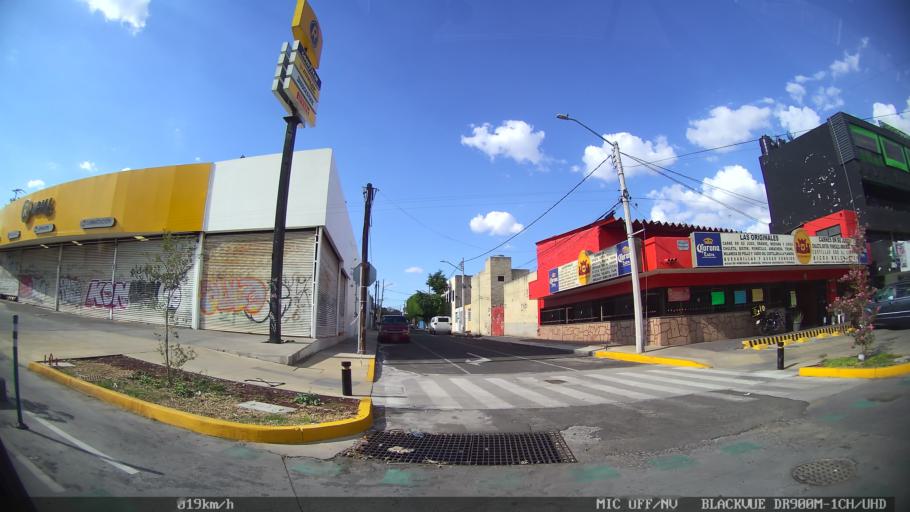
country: MX
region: Jalisco
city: Tlaquepaque
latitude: 20.6620
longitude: -103.3277
